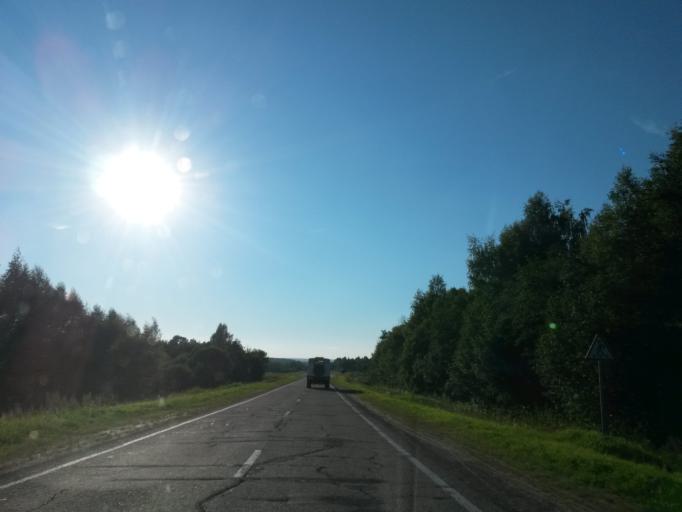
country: RU
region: Jaroslavl
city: Gavrilov-Yam
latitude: 57.2753
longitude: 39.9343
